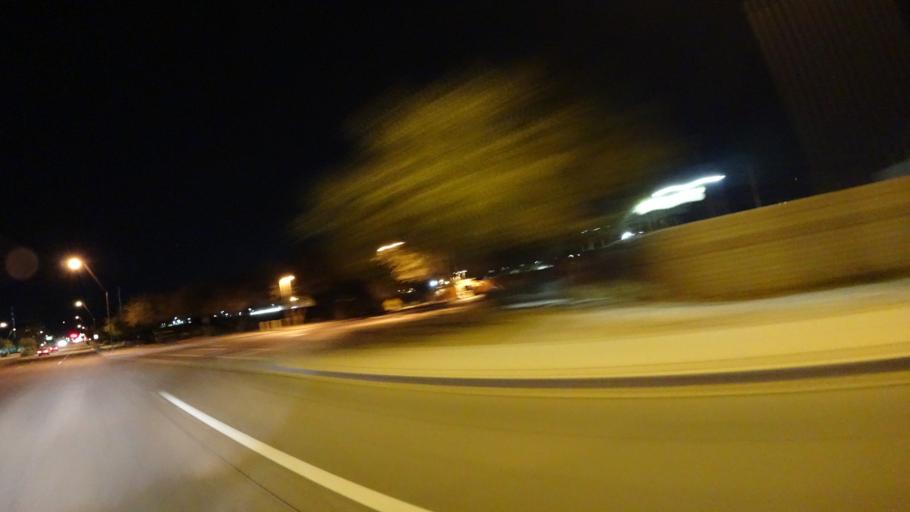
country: US
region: Arizona
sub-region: Maricopa County
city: Guadalupe
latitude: 33.3493
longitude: -111.9411
